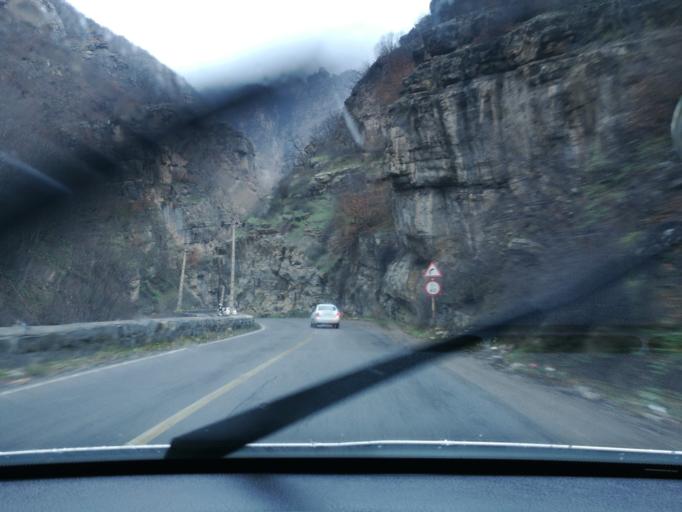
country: IR
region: Mazandaran
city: Chalus
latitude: 36.2695
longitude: 51.2506
